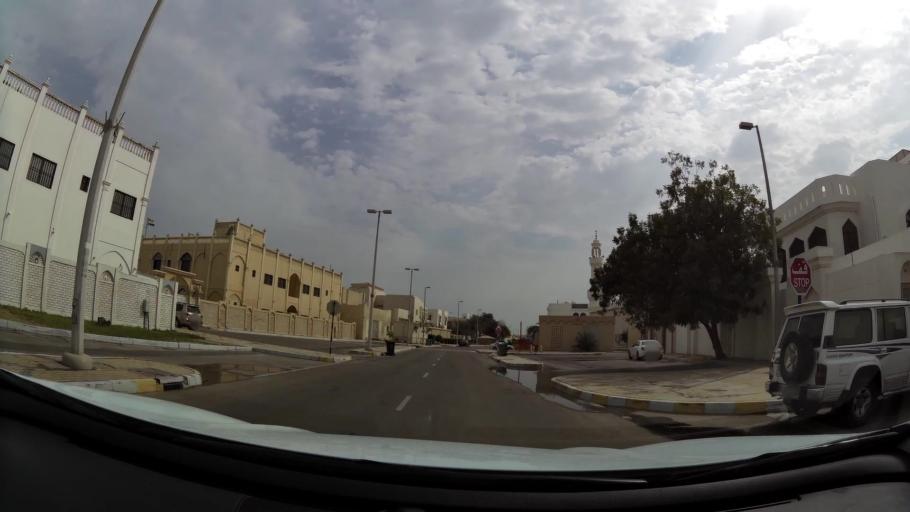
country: AE
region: Abu Dhabi
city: Abu Dhabi
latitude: 24.4440
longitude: 54.4341
